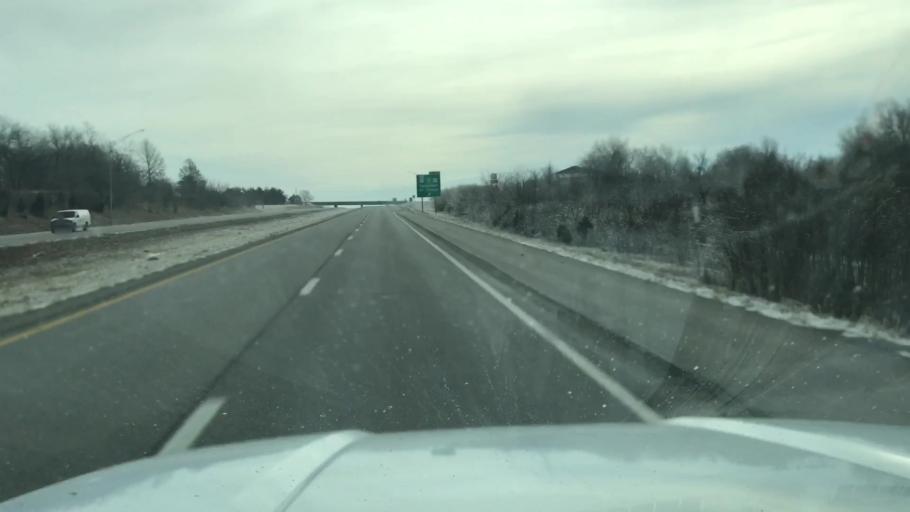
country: US
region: Missouri
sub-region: Andrew County
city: Country Club Village
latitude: 39.8619
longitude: -94.8171
